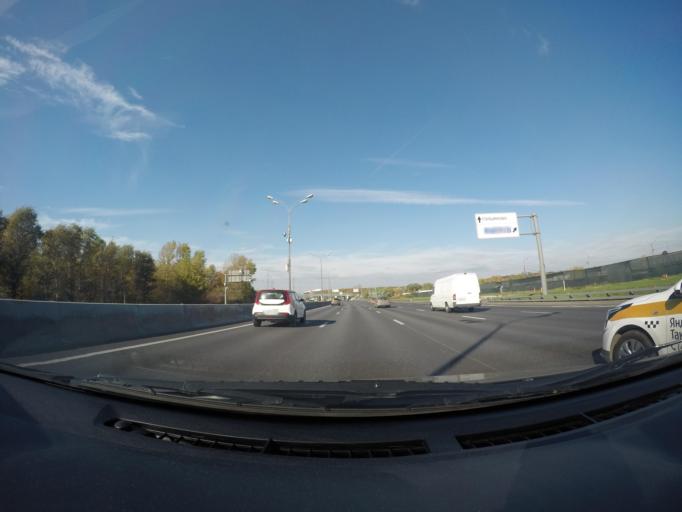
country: RU
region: Moscow
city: Gol'yanovo
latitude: 55.8271
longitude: 37.8327
